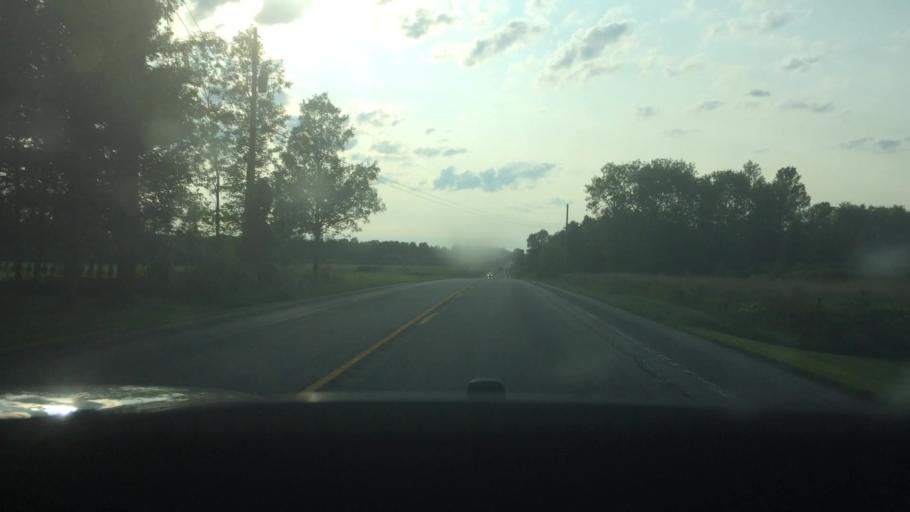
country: US
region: New York
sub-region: St. Lawrence County
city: Ogdensburg
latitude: 44.6715
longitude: -75.3861
